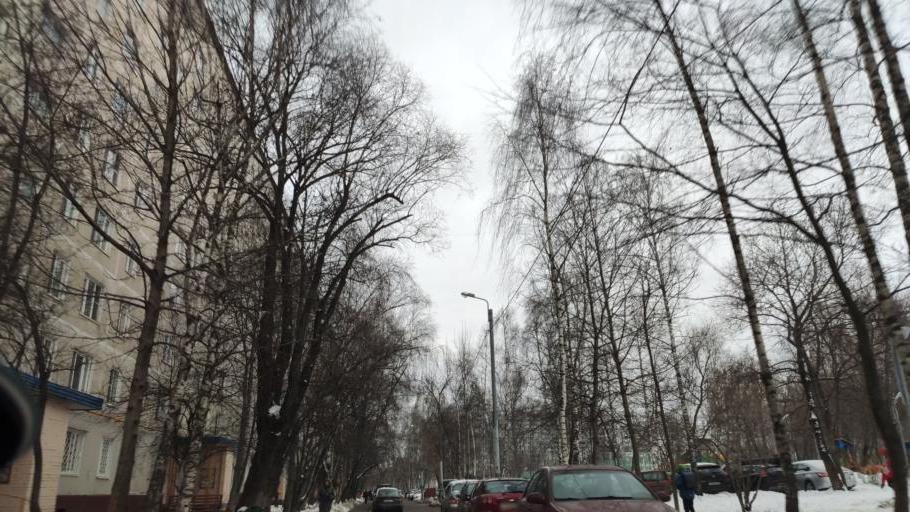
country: RU
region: Moscow
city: Tyoply Stan
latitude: 55.6198
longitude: 37.4910
